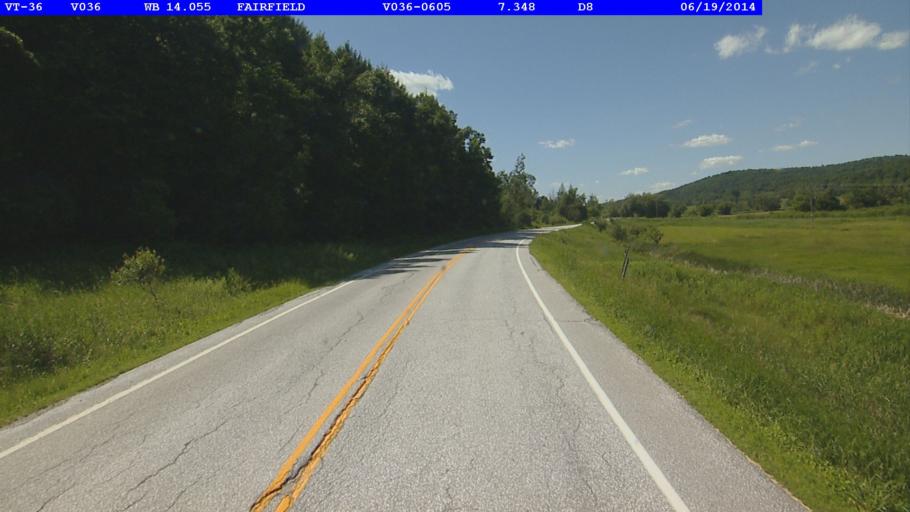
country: US
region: Vermont
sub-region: Franklin County
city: Enosburg Falls
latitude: 44.8005
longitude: -72.8934
